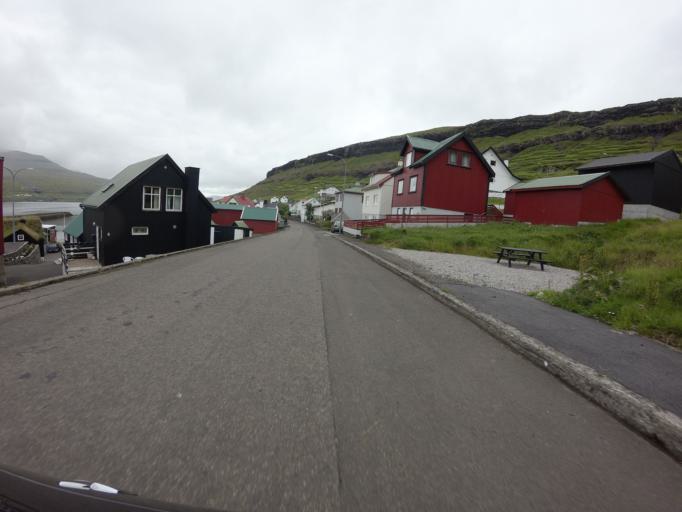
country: FO
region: Eysturoy
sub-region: Eidi
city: Eidi
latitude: 62.2757
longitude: -7.0941
